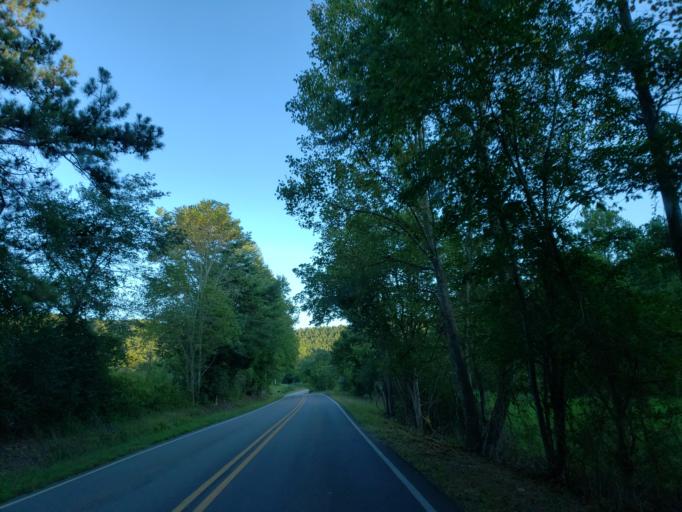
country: US
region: Georgia
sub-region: Bartow County
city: Rydal
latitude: 34.3691
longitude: -84.5821
